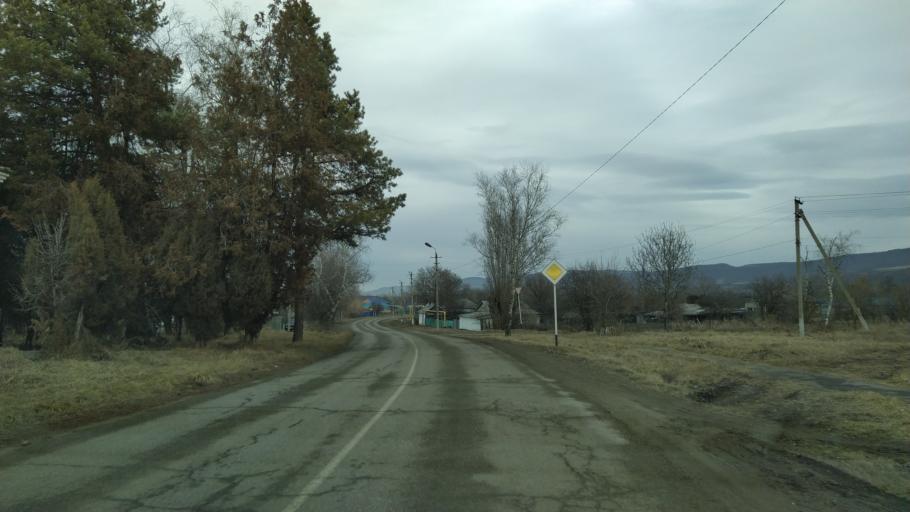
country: RU
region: Krasnodarskiy
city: Peredovaya
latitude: 44.1261
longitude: 41.4795
